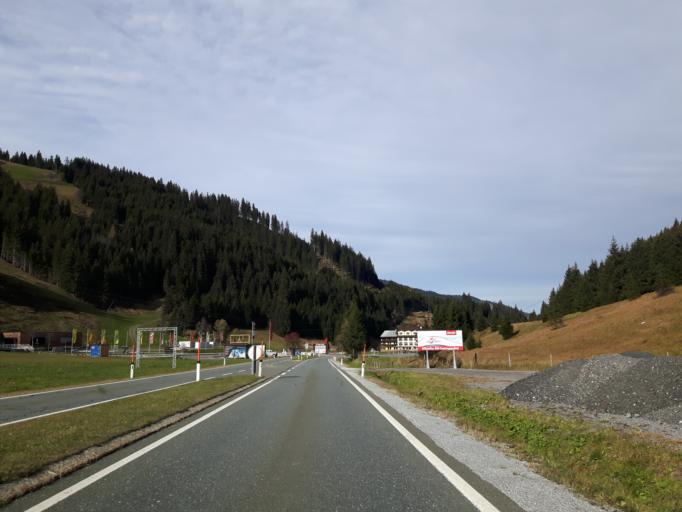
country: AT
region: Salzburg
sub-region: Politischer Bezirk Zell am See
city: Hollersbach im Pinzgau
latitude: 47.3191
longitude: 12.4081
